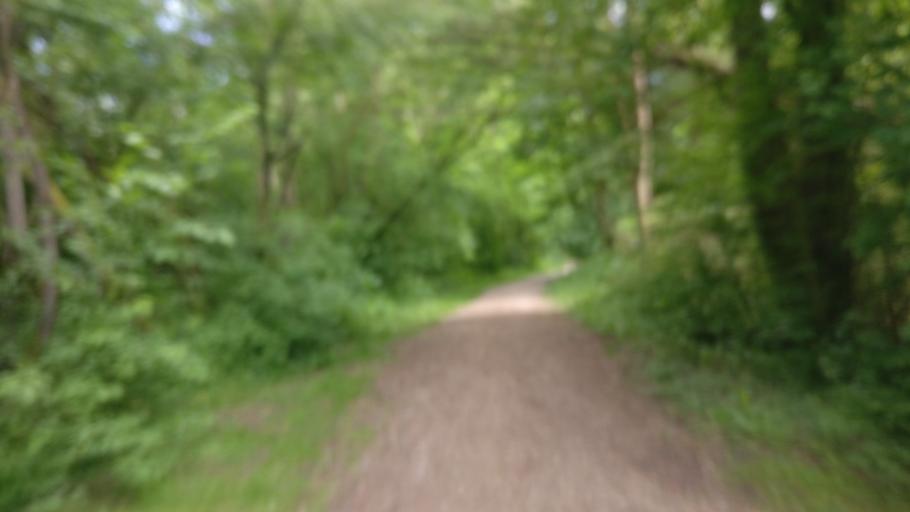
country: DE
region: North Rhine-Westphalia
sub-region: Regierungsbezirk Detmold
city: Lage
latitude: 52.0073
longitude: 8.7650
